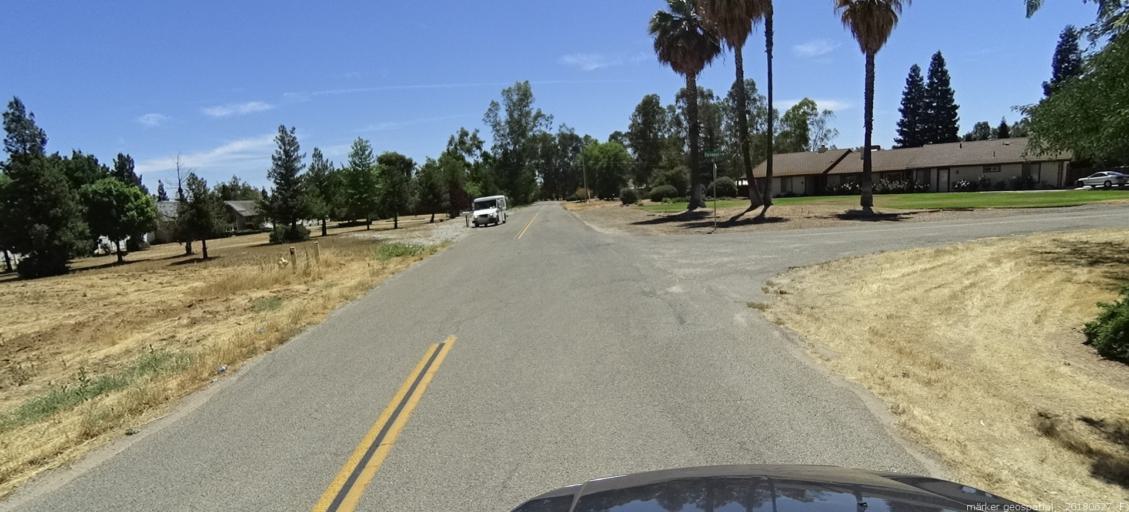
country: US
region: California
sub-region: Madera County
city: Bonadelle Ranchos-Madera Ranchos
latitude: 36.9329
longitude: -119.8691
